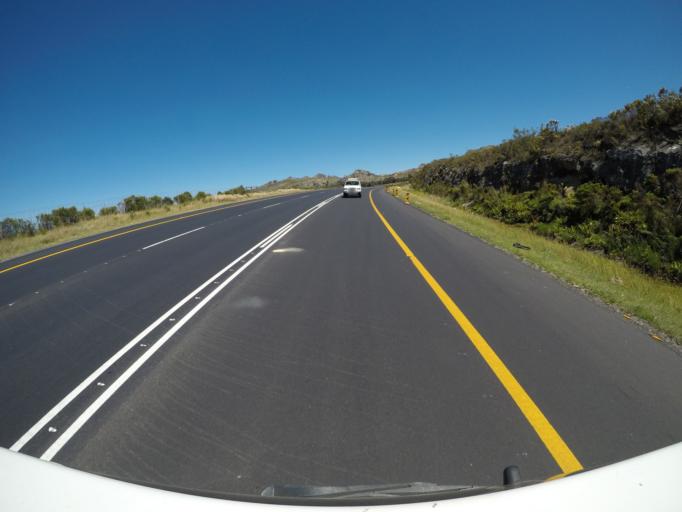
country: ZA
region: Western Cape
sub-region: Overberg District Municipality
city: Grabouw
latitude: -34.1529
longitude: 18.9398
